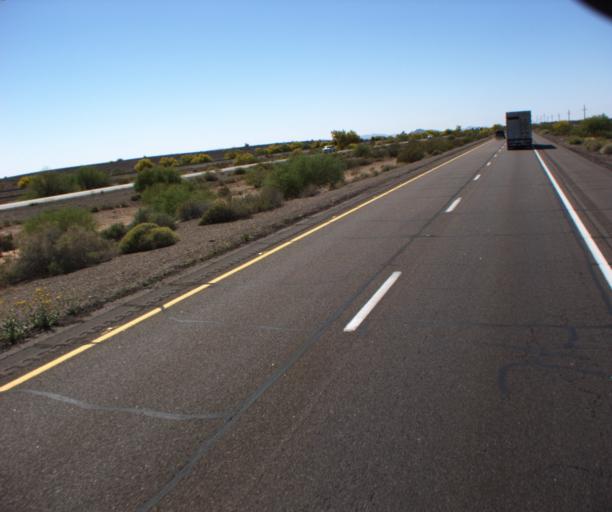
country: US
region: Arizona
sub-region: Maricopa County
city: Gila Bend
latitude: 32.8418
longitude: -113.3108
